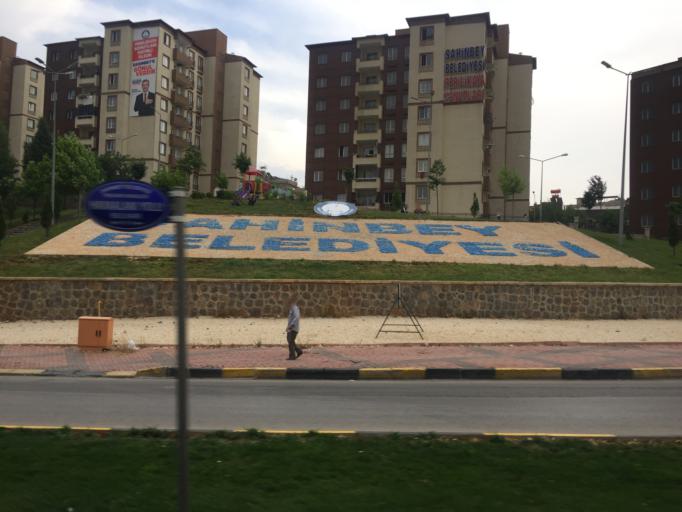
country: TR
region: Gaziantep
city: Gaziantep
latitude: 37.0550
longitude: 37.4158
